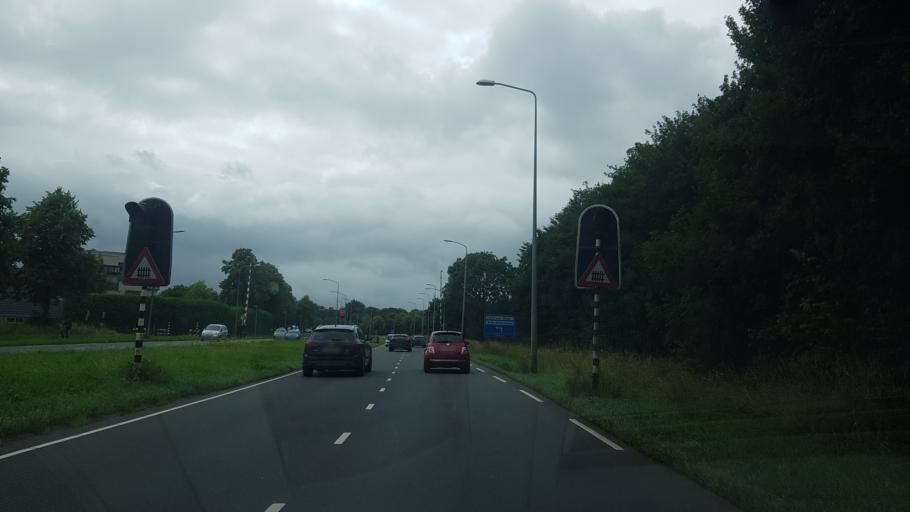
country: NL
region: North Holland
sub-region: Gemeente Hoorn
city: Hoorn
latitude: 52.6538
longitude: 5.0716
